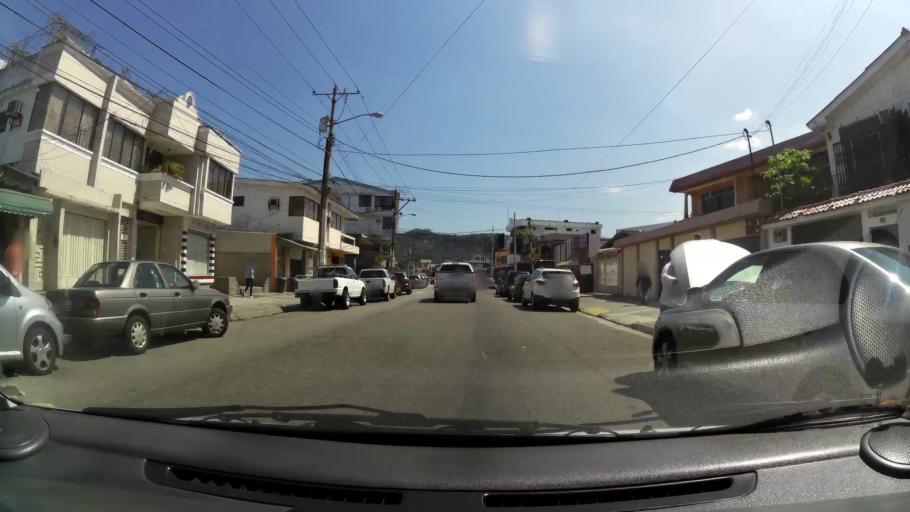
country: EC
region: Guayas
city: Guayaquil
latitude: -2.1655
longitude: -79.9105
